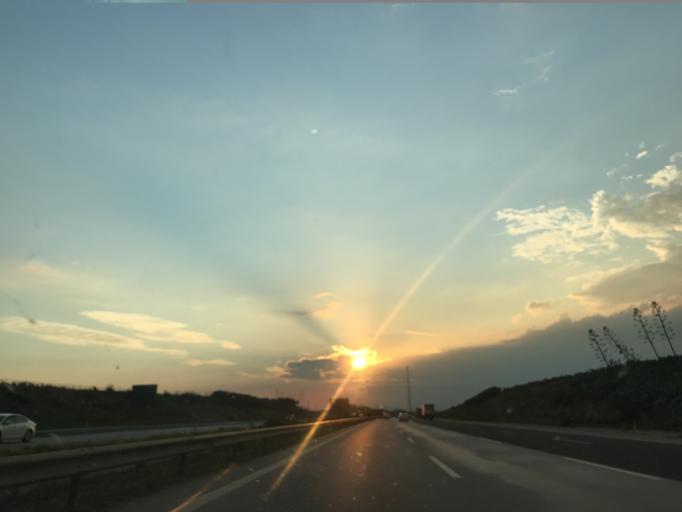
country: TR
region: Mersin
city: Yenice
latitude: 37.0243
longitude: 35.1007
